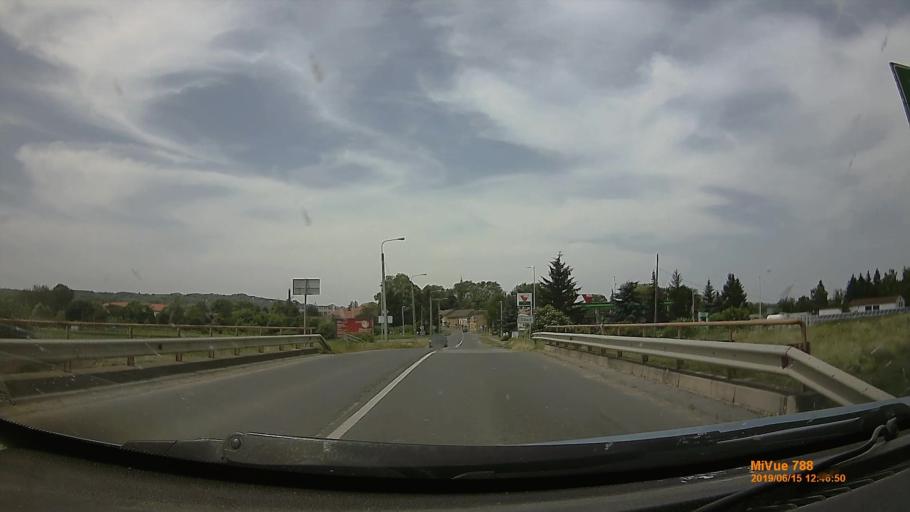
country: HU
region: Baranya
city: Sasd
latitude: 46.2510
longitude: 18.1167
